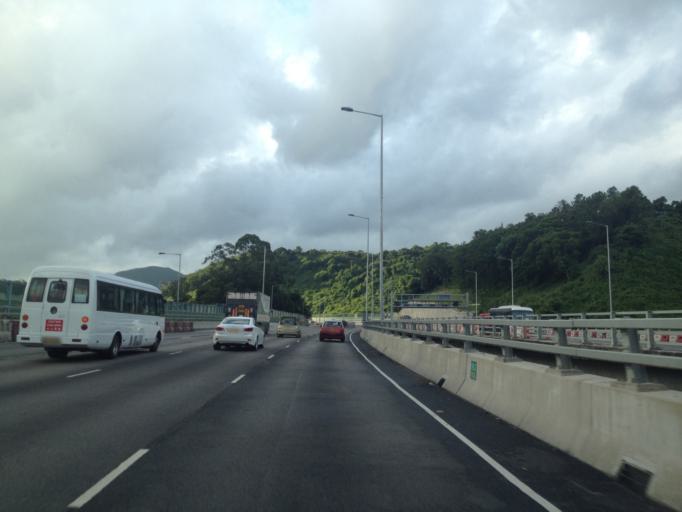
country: HK
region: Tai Po
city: Tai Po
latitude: 22.4501
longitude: 114.1539
